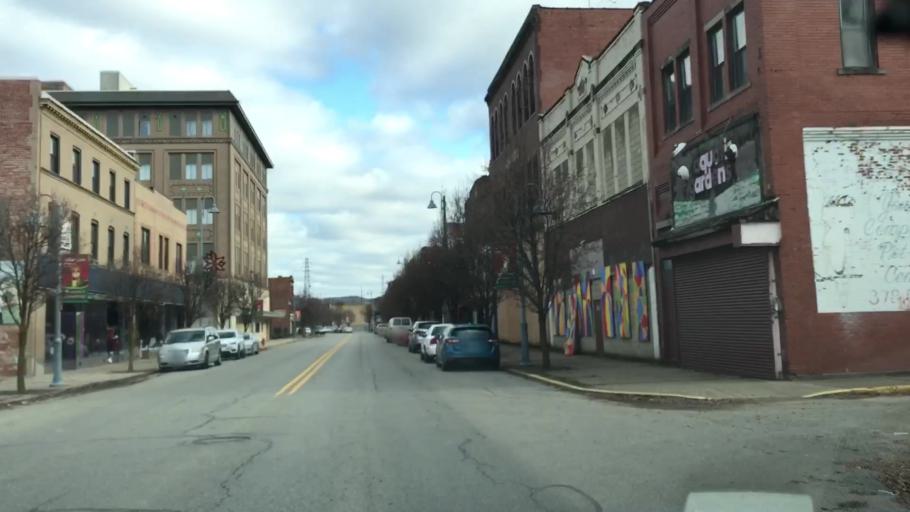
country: US
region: Pennsylvania
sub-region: Beaver County
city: Aliquippa
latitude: 40.6155
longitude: -80.2485
